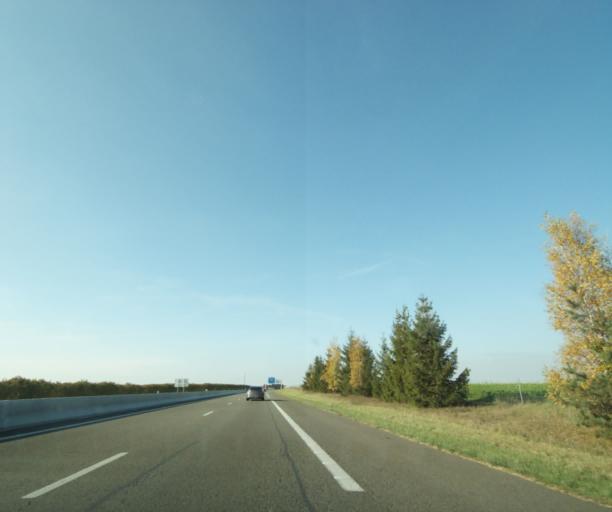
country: FR
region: Champagne-Ardenne
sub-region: Departement de la Marne
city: Courtisols
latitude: 49.0339
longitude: 4.4499
